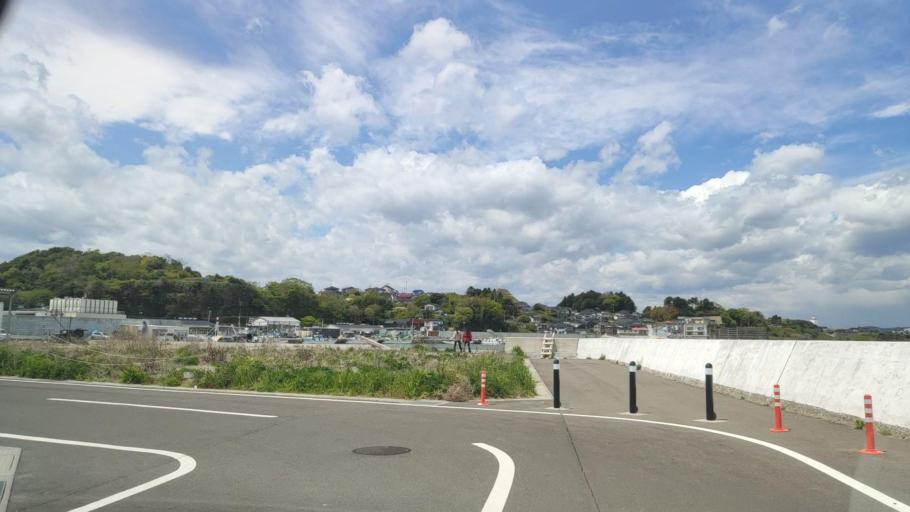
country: JP
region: Miyagi
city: Shiogama
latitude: 38.3049
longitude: 141.0848
